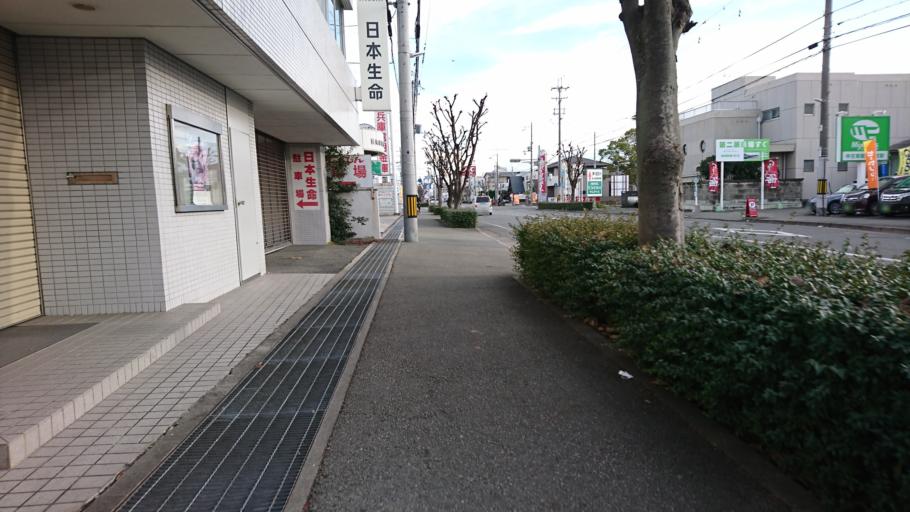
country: JP
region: Hyogo
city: Kakogawacho-honmachi
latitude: 34.7558
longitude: 134.8363
